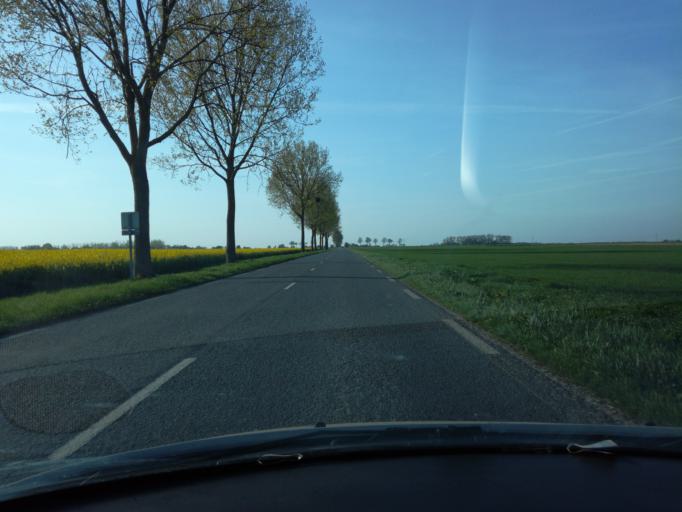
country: FR
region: Picardie
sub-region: Departement de la Somme
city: Poix-de-Picardie
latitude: 49.8166
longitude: 1.9599
